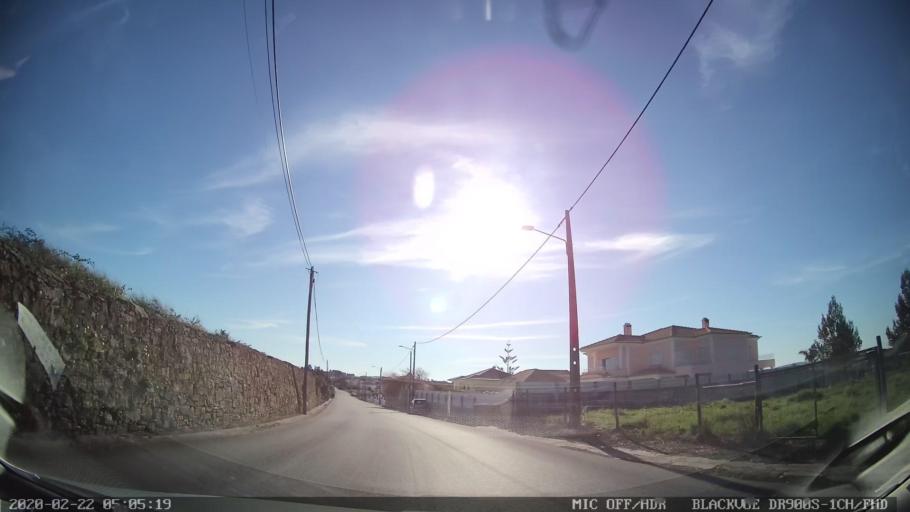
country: PT
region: Lisbon
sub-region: Vila Franca de Xira
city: Vila Franca de Xira
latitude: 38.9730
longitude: -9.0065
